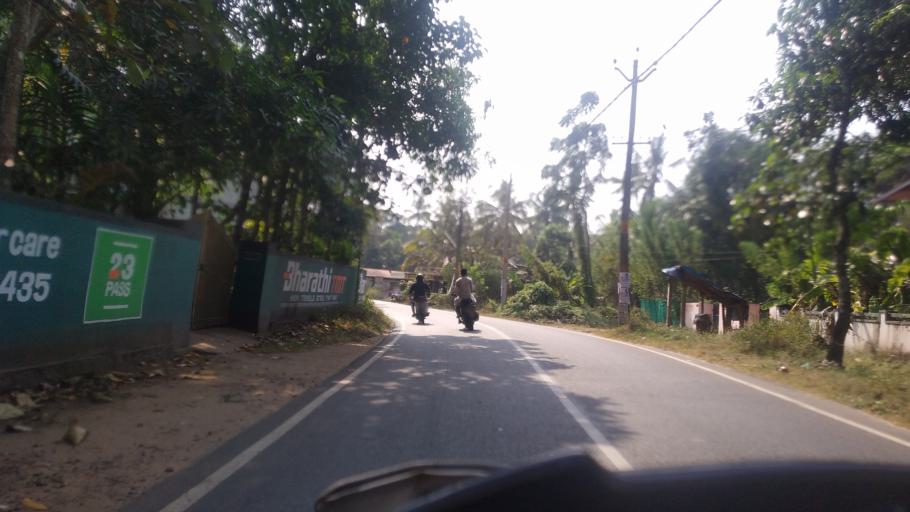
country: IN
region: Kerala
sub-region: Thrissur District
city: Kodungallur
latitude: 10.2091
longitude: 76.1862
